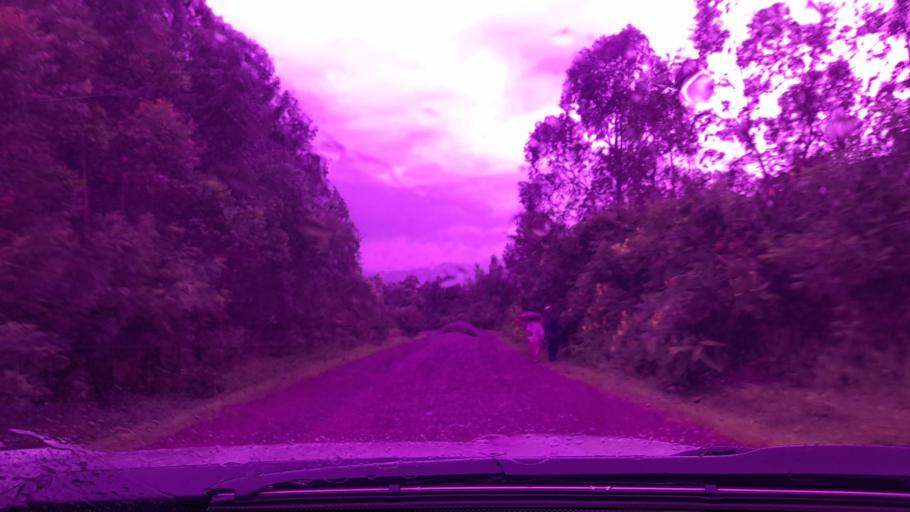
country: ET
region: Oromiya
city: Metu
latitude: 8.4333
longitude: 35.6150
